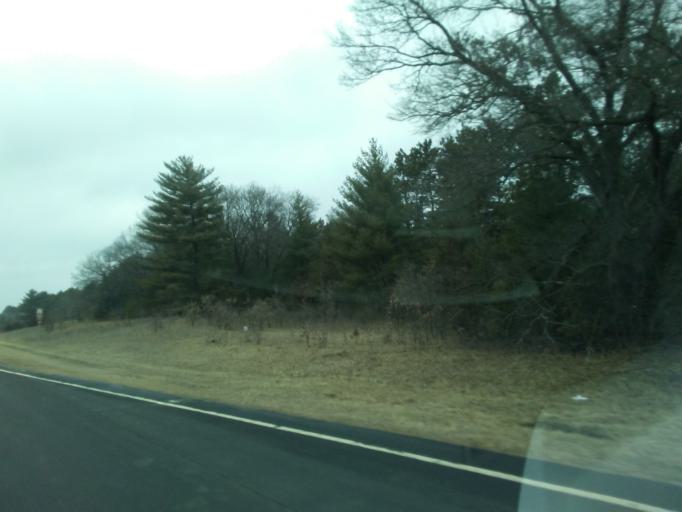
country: US
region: Wisconsin
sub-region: Sauk County
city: Spring Green
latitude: 43.1933
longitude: -90.2259
